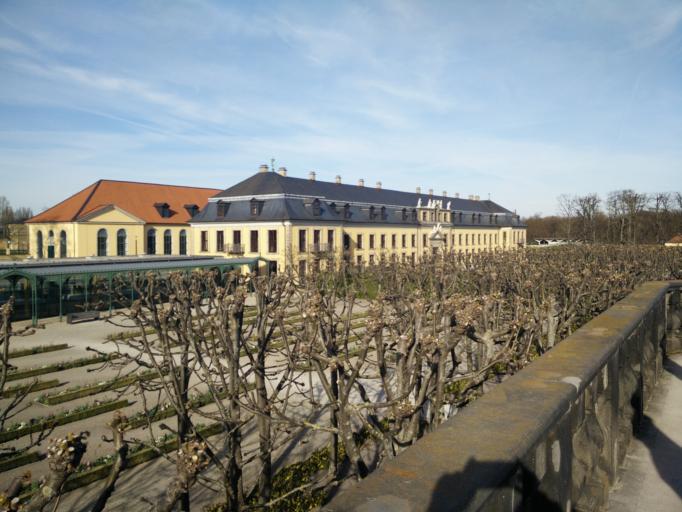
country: DE
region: Lower Saxony
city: Hannover
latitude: 52.3906
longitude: 9.6983
